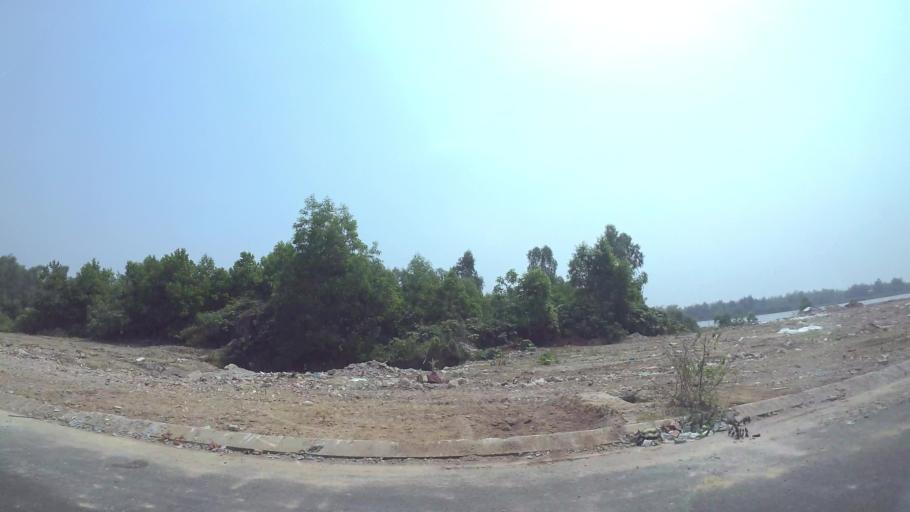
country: VN
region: Da Nang
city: Cam Le
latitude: 15.9806
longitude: 108.2203
